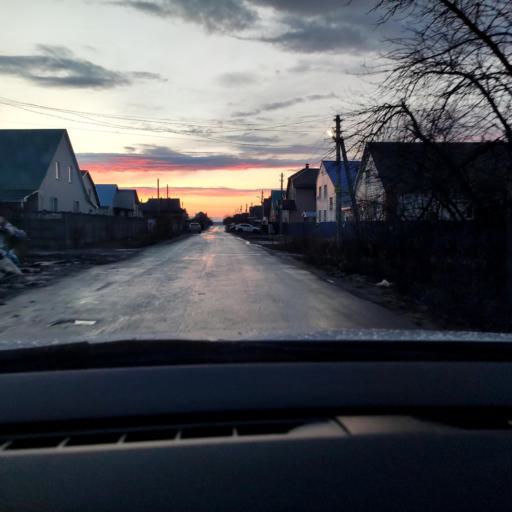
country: RU
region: Voronezj
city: Semiluki
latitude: 51.7113
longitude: 39.0254
